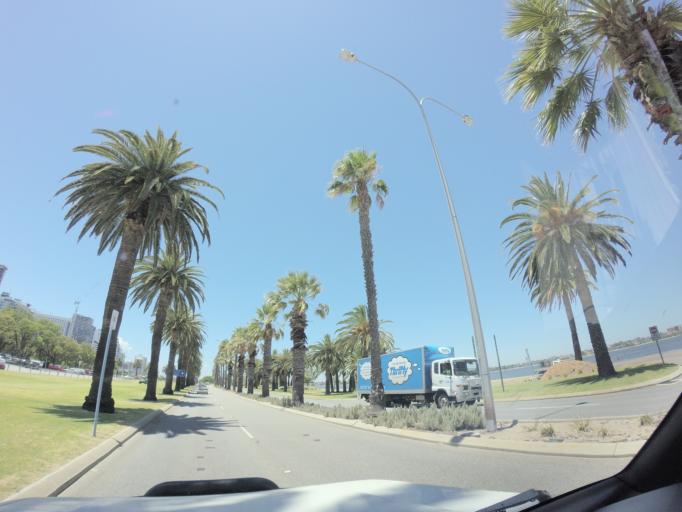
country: AU
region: Western Australia
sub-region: Cambridge
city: Perth
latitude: -31.9597
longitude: 115.8619
